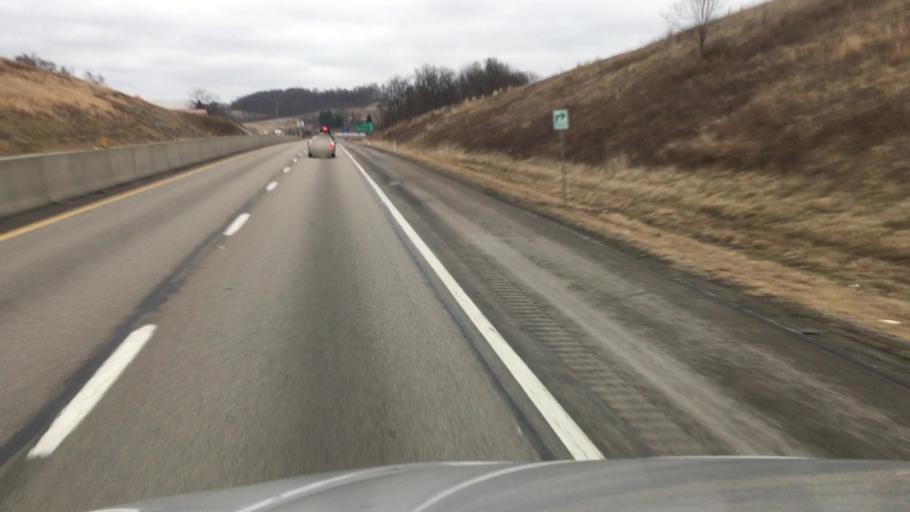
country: US
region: Pennsylvania
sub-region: Westmoreland County
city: West Newton
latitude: 40.1660
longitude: -79.7426
